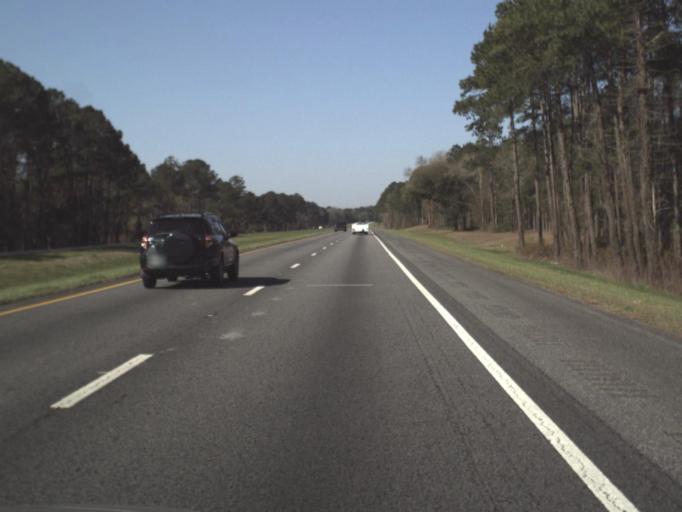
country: US
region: Florida
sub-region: Jefferson County
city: Monticello
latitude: 30.4816
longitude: -84.0510
